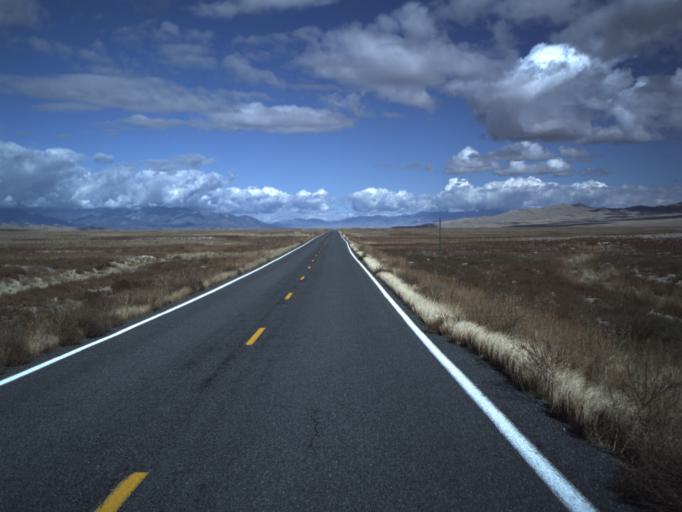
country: US
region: Utah
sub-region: Beaver County
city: Milford
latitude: 38.6352
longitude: -113.8573
